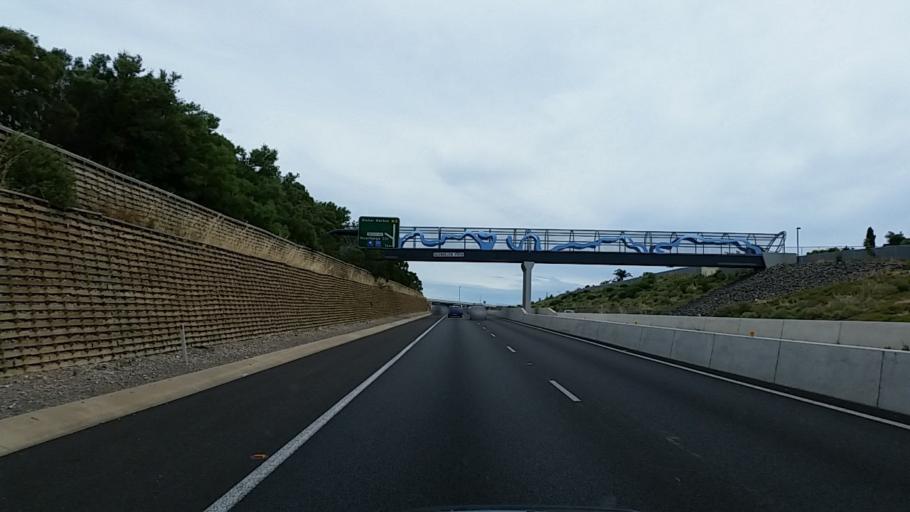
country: AU
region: South Australia
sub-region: Onkaparinga
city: Morphett Vale
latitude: -35.1234
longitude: 138.5071
